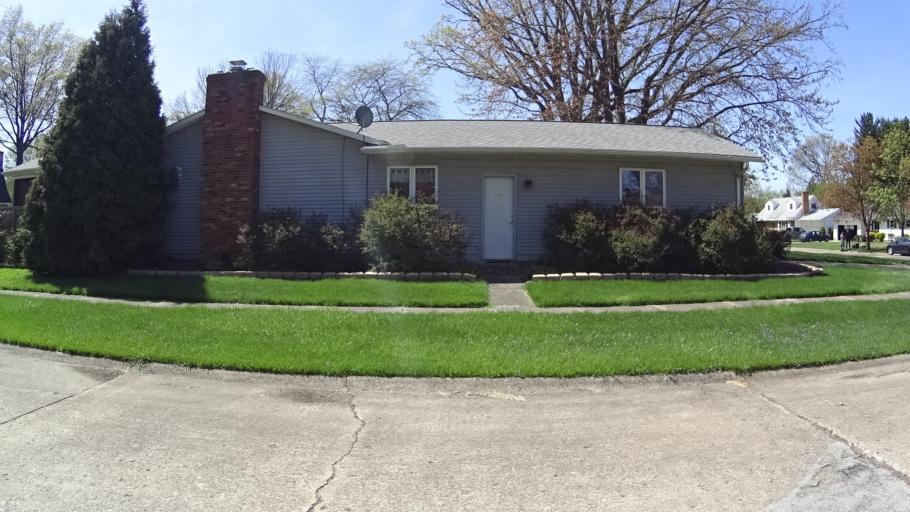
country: US
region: Ohio
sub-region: Lorain County
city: Elyria
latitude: 41.3766
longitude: -82.0969
